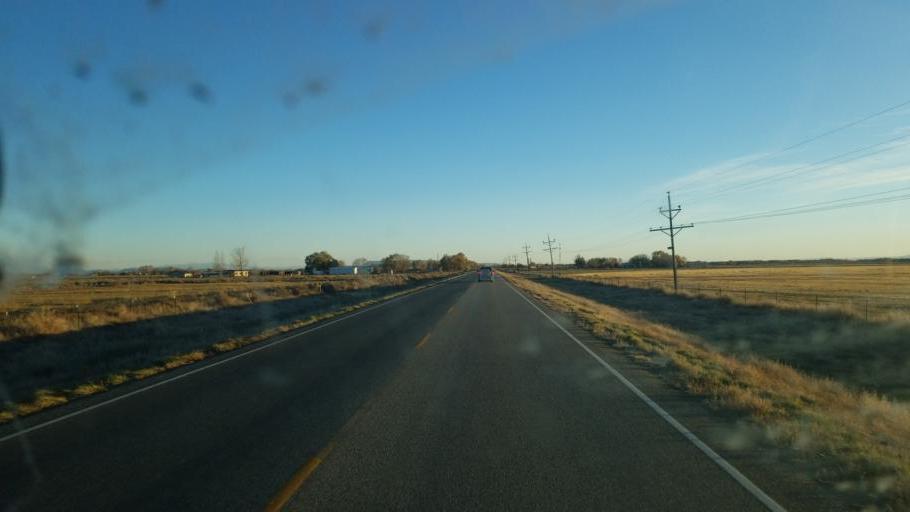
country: US
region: Colorado
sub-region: Alamosa County
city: Alamosa East
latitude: 37.5132
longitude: -105.8586
